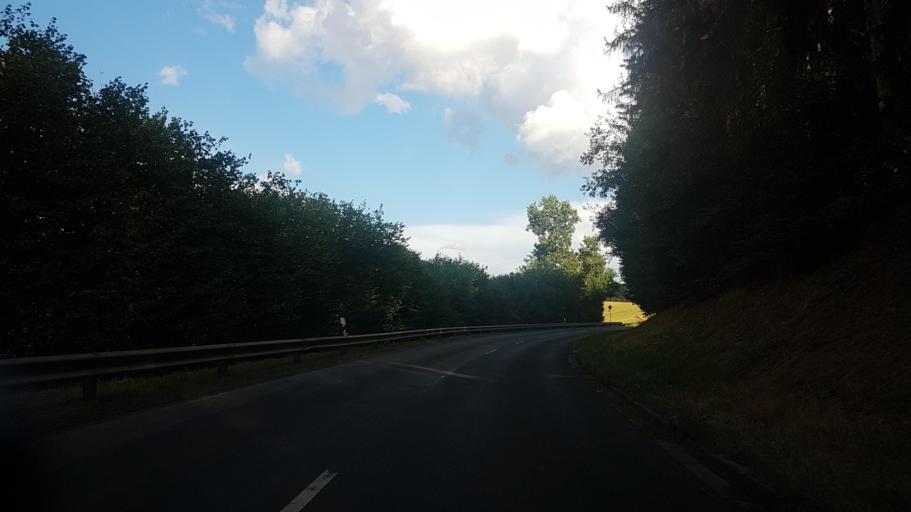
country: DE
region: Rheinland-Pfalz
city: Dienstweiler
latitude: 49.6363
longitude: 7.1919
